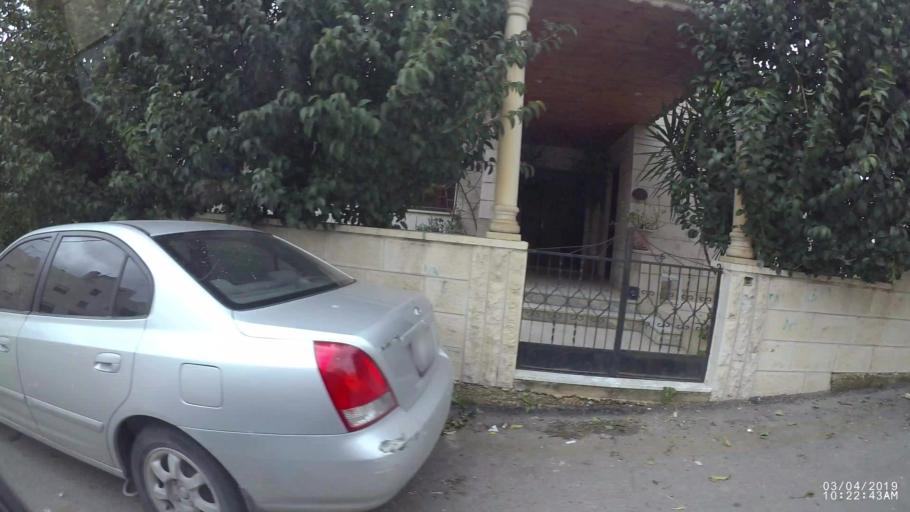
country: JO
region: Amman
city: Wadi as Sir
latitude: 31.9469
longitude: 35.8245
